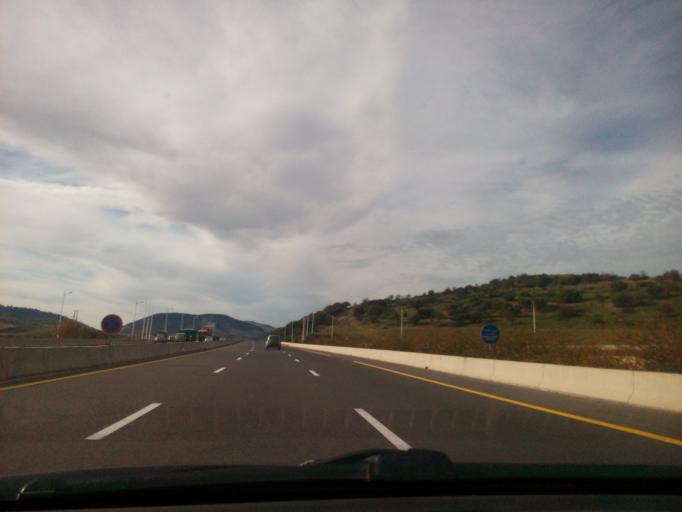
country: DZ
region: Sidi Bel Abbes
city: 'Ain el Berd
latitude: 35.4315
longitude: -0.4580
